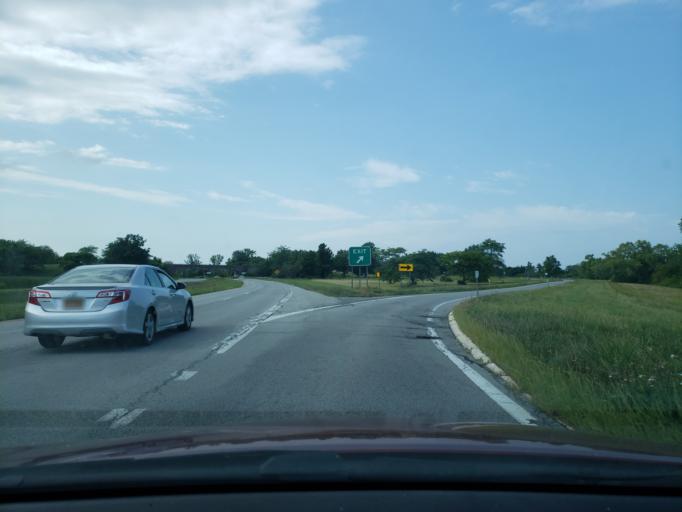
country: US
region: New York
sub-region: Monroe County
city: Greece
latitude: 43.2788
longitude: -77.6936
